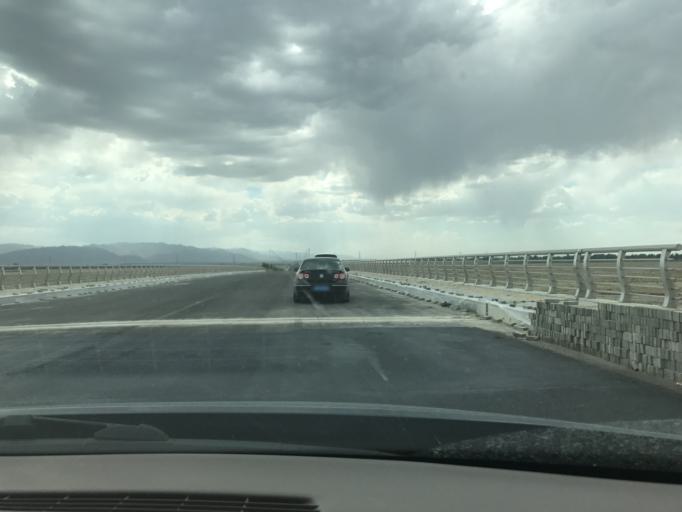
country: CN
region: Gansu Sheng
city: Wuwei
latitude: 38.1032
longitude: 102.4195
